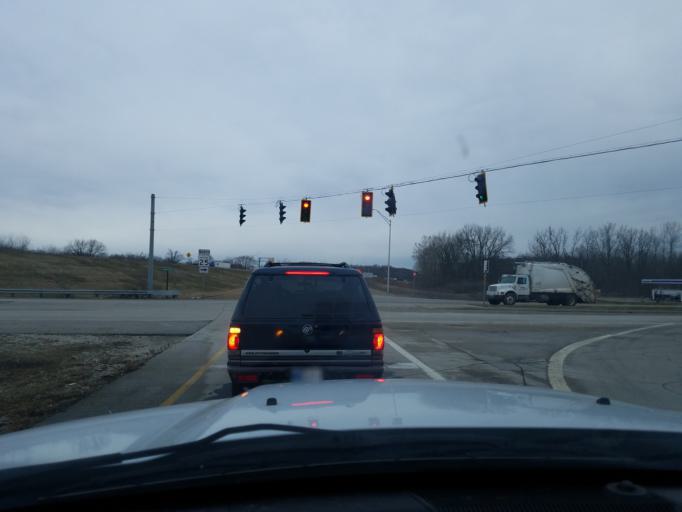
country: US
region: Indiana
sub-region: Tippecanoe County
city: Lafayette
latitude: 40.4563
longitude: -86.8463
